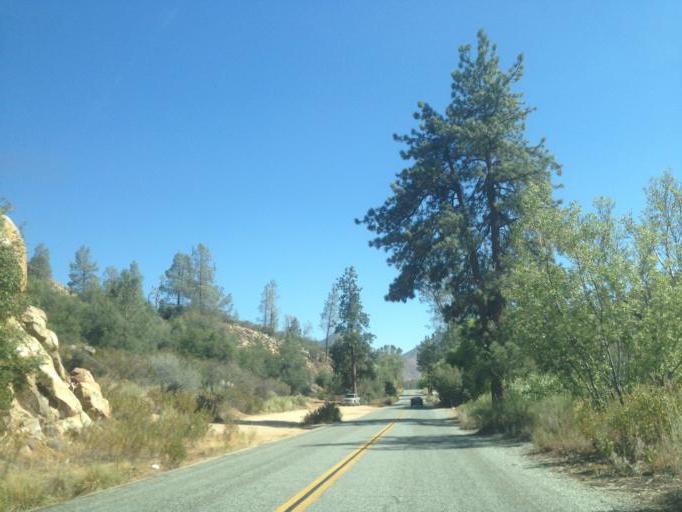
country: US
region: California
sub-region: Kern County
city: Kernville
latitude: 35.8982
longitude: -118.4675
